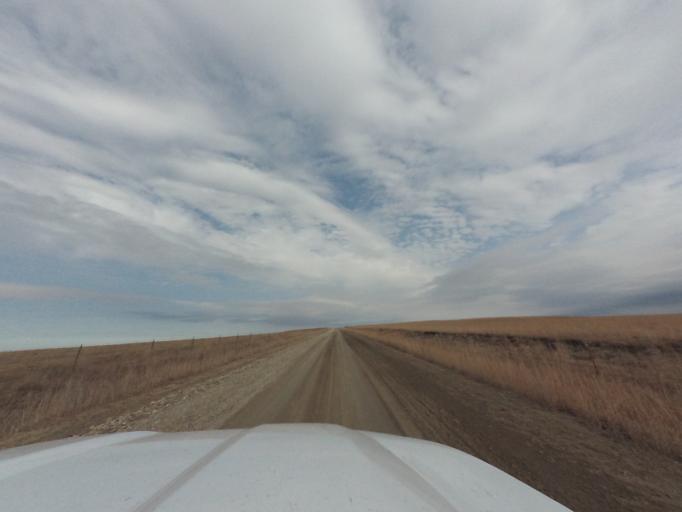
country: US
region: Kansas
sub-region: Chase County
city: Cottonwood Falls
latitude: 38.2277
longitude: -96.7307
